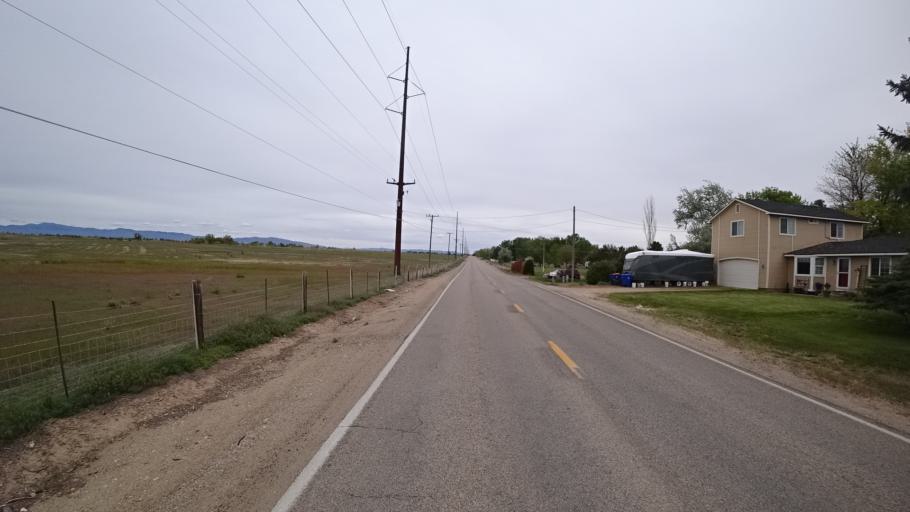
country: US
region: Idaho
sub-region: Ada County
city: Kuna
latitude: 43.4882
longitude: -116.3327
